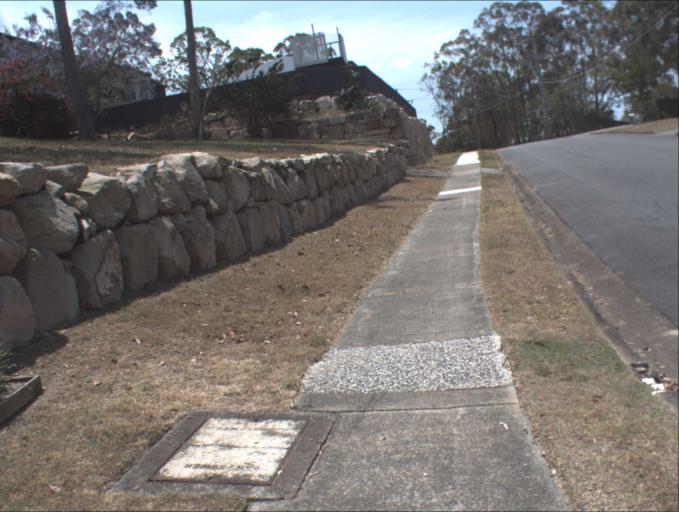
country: AU
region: Queensland
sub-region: Logan
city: Beenleigh
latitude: -27.6651
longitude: 153.1988
